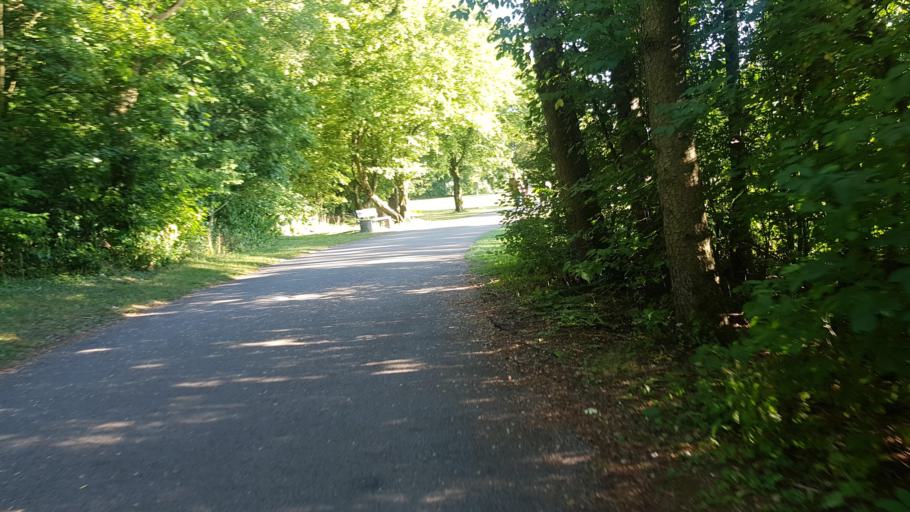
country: DE
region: Bavaria
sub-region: Upper Bavaria
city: Karlsfeld
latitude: 48.2379
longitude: 11.4719
